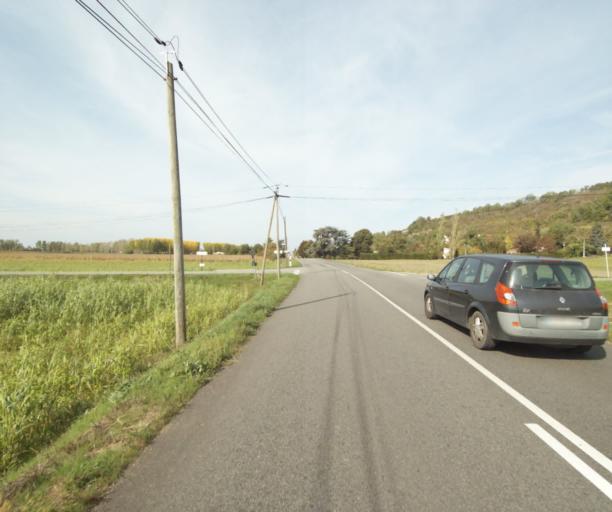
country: FR
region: Midi-Pyrenees
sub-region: Departement du Tarn-et-Garonne
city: Corbarieu
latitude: 43.9375
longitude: 1.3758
